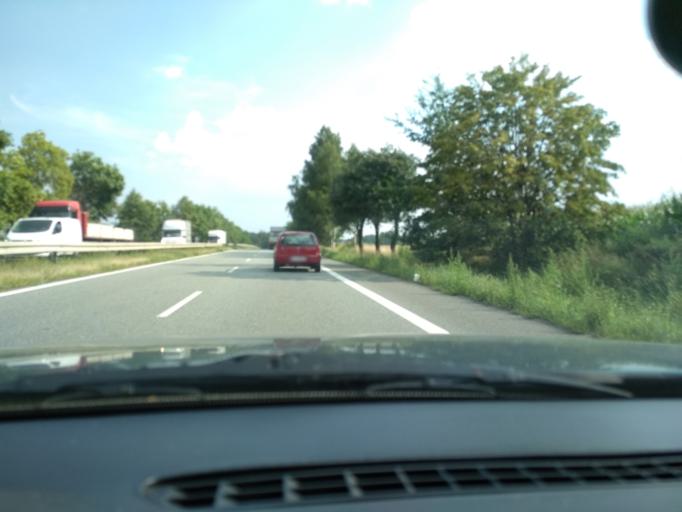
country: PL
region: Silesian Voivodeship
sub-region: Powiat pszczynski
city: Krzyzowice
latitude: 50.0030
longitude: 18.7105
